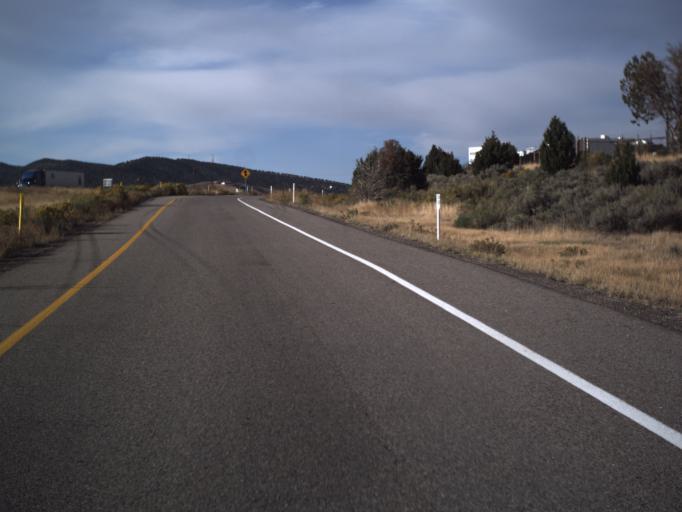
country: US
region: Utah
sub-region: Washington County
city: Toquerville
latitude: 37.4828
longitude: -113.2196
